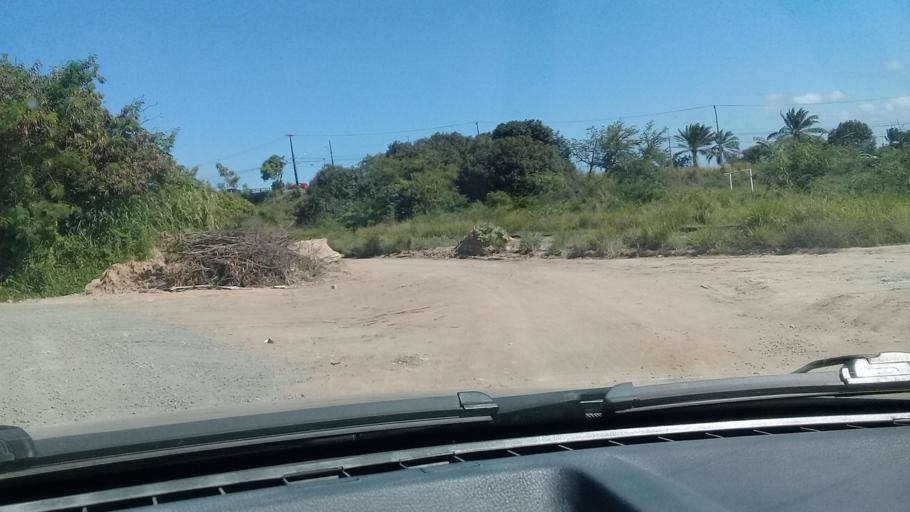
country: BR
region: Pernambuco
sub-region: Jaboatao Dos Guararapes
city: Jaboatao
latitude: -8.1533
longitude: -34.9509
